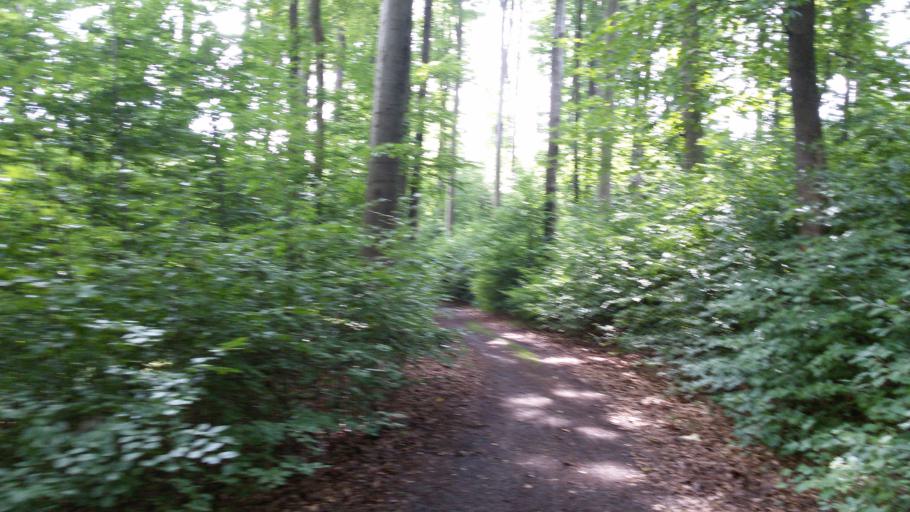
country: CZ
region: Vysocina
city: Heralec
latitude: 49.6561
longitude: 15.9970
